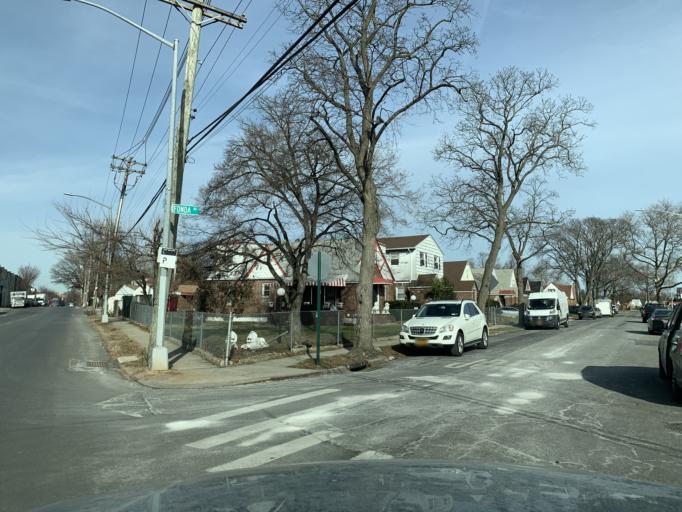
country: US
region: New York
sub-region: Queens County
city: Jamaica
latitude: 40.6998
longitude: -73.7718
